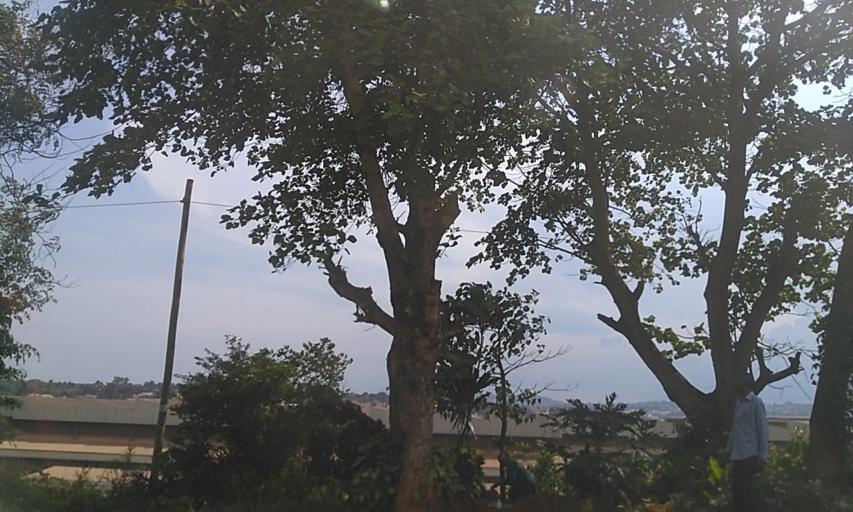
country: UG
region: Central Region
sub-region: Kampala District
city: Kampala
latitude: 0.2945
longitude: 32.5545
